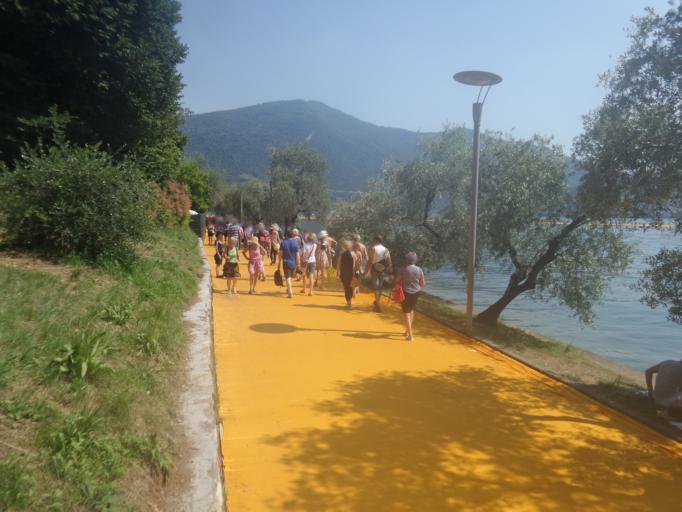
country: IT
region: Lombardy
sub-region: Provincia di Brescia
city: Siviano
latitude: 45.6970
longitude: 10.0823
